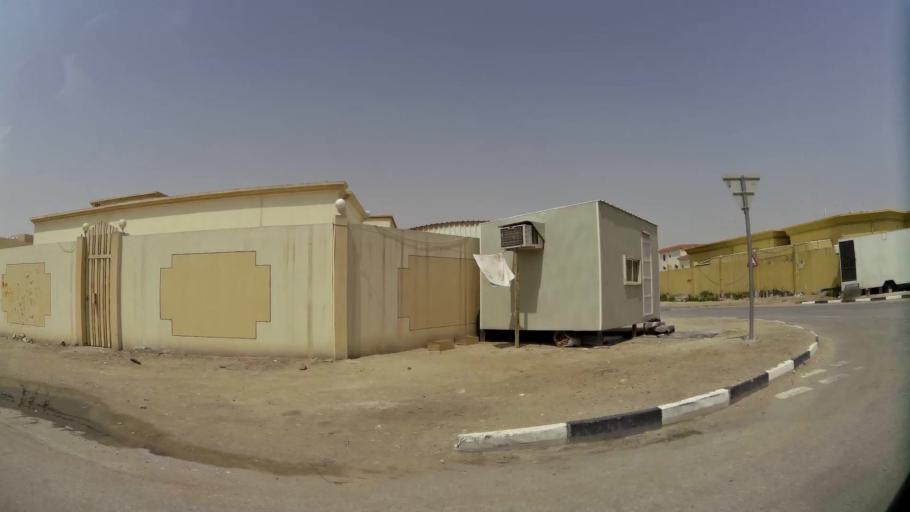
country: QA
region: Baladiyat ar Rayyan
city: Ar Rayyan
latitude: 25.2290
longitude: 51.4154
